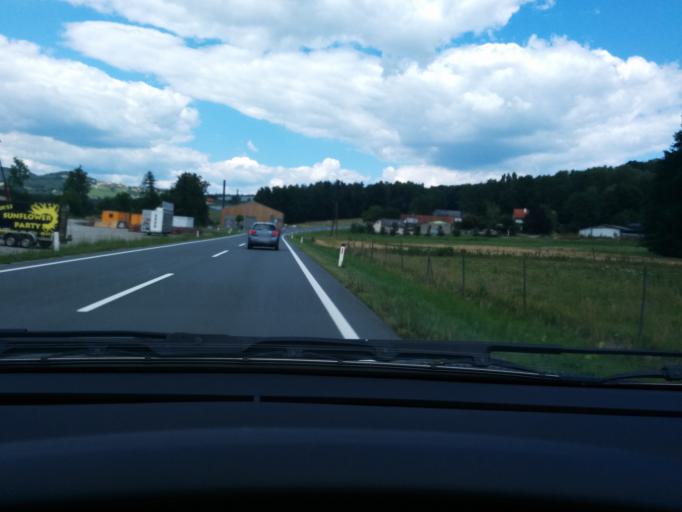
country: AT
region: Styria
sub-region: Politischer Bezirk Weiz
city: Hirnsdorf
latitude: 47.1790
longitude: 15.8103
